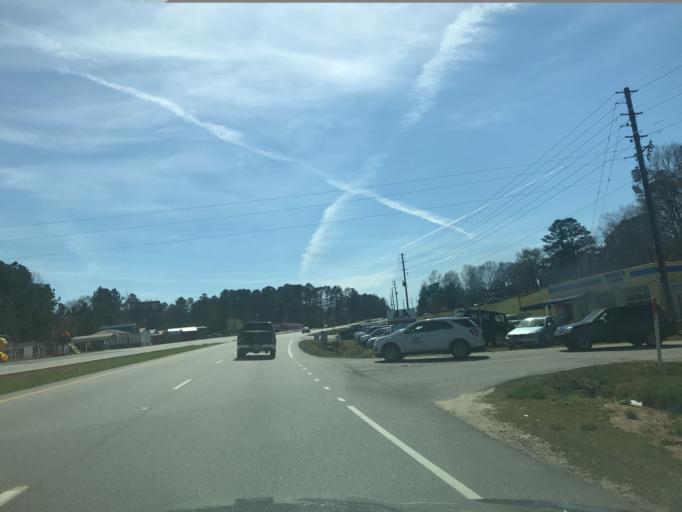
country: US
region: North Carolina
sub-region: Wake County
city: Fuquay-Varina
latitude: 35.6303
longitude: -78.7168
